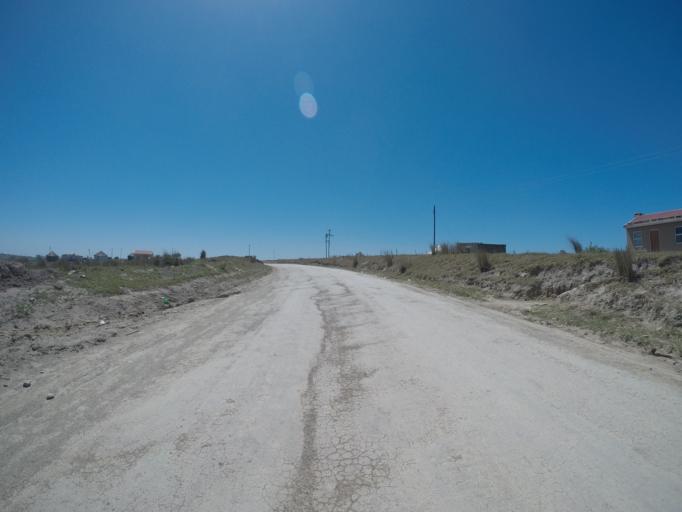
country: ZA
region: Eastern Cape
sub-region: OR Tambo District Municipality
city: Libode
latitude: -31.9384
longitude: 29.0285
